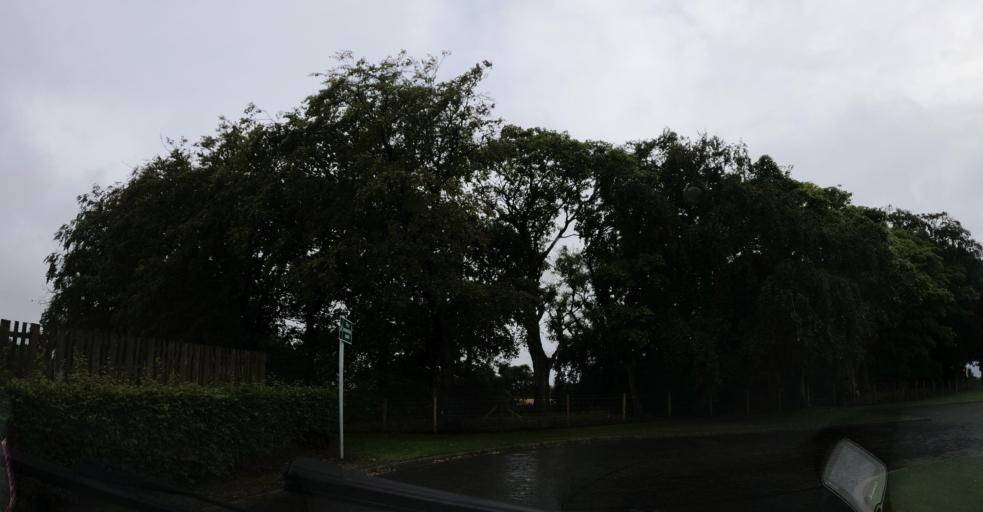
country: GB
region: Scotland
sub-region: West Lothian
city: West Calder
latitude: 55.8506
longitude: -3.5562
